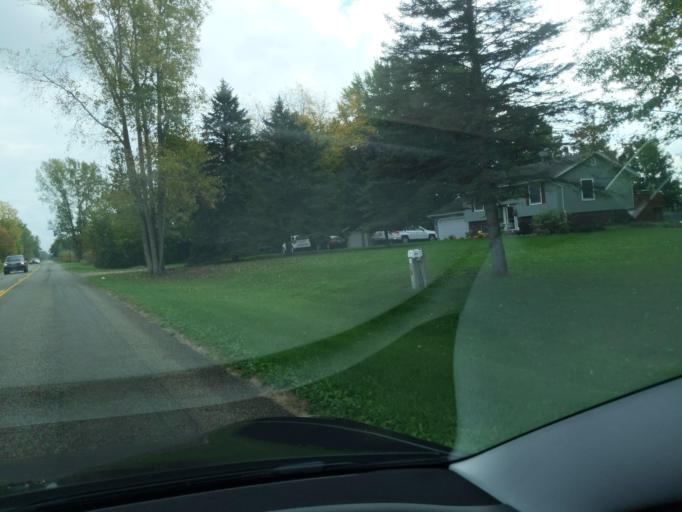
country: US
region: Michigan
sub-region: Eaton County
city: Eaton Rapids
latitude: 42.4808
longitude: -84.6358
